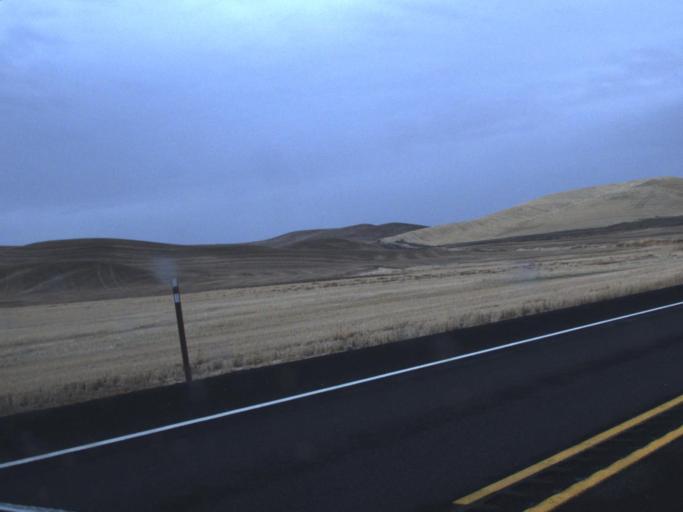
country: US
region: Washington
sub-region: Whitman County
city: Pullman
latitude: 46.6417
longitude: -117.1838
